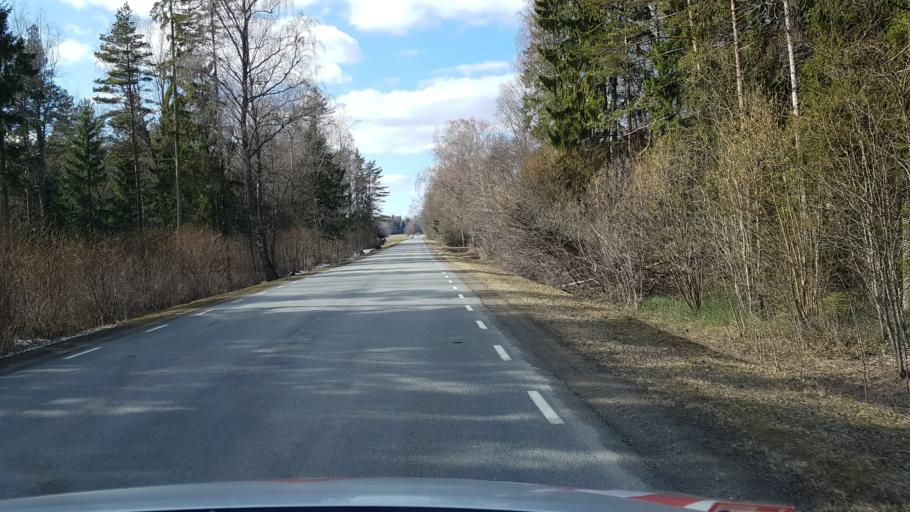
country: EE
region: Laeaene-Virumaa
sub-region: Tamsalu vald
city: Tamsalu
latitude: 59.1651
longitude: 26.0775
